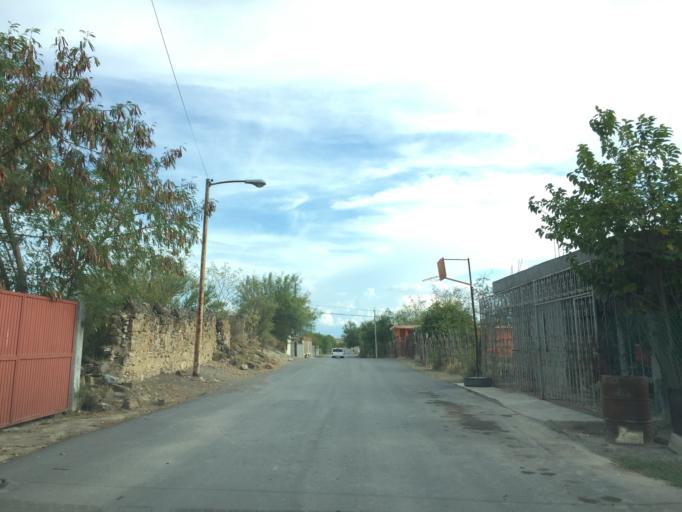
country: MX
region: Nuevo Leon
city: Marin
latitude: 25.8589
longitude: -99.9457
